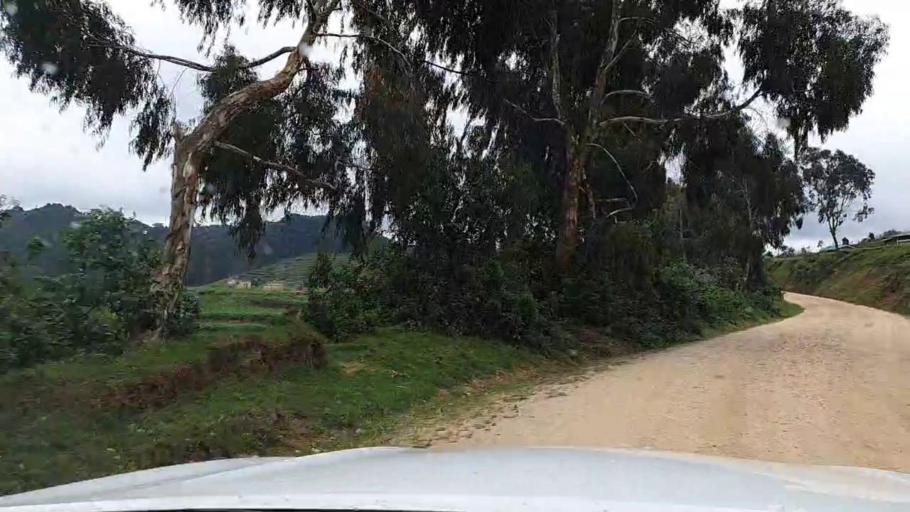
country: RW
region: Southern Province
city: Nzega
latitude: -2.3753
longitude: 29.3808
